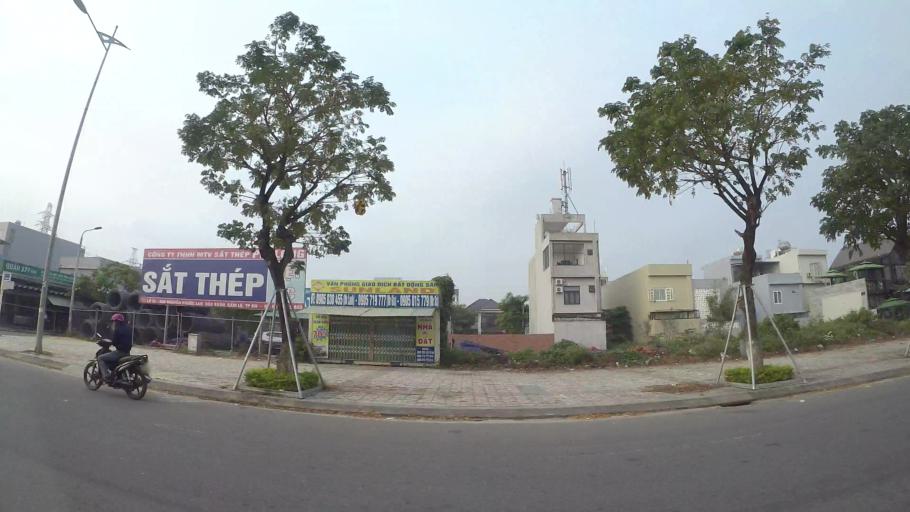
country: VN
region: Da Nang
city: Cam Le
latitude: 16.0198
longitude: 108.2285
